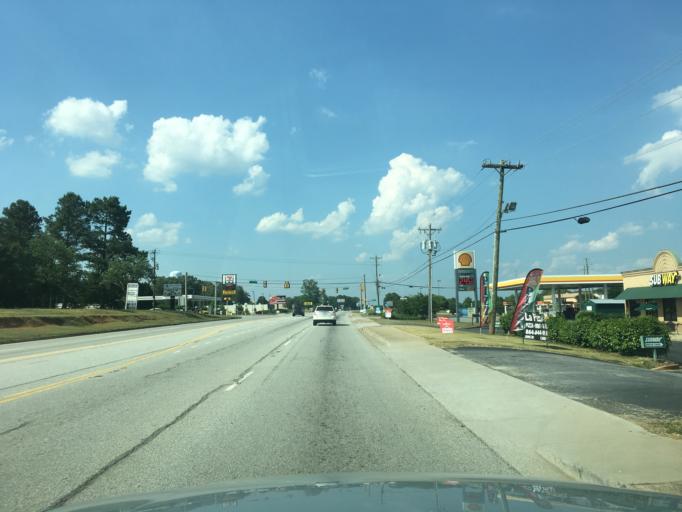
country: US
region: South Carolina
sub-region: Anderson County
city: Northlake
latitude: 34.5960
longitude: -82.6169
